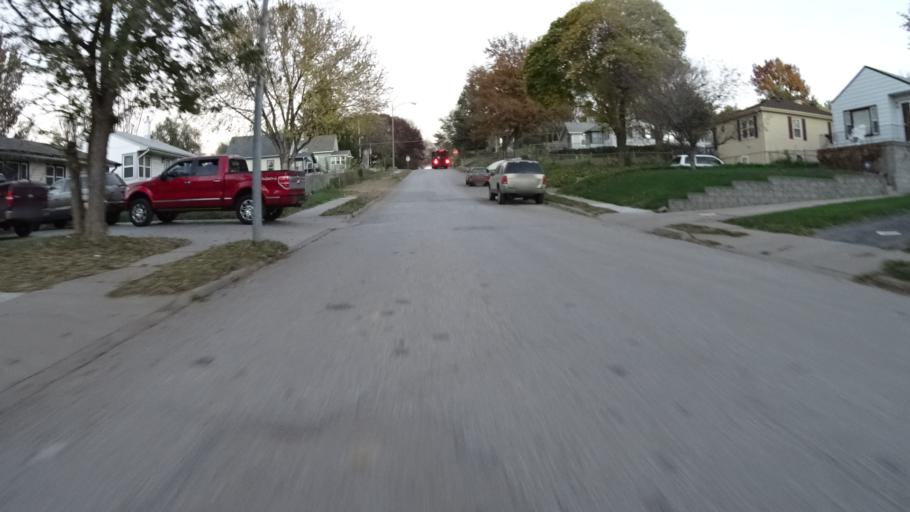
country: US
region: Nebraska
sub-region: Douglas County
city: Omaha
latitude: 41.1919
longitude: -95.9469
